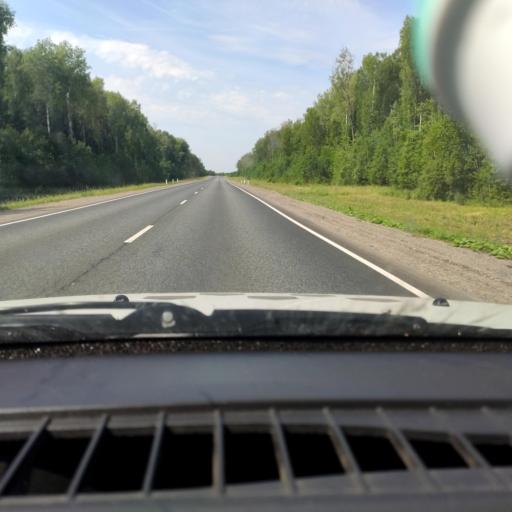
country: RU
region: Kirov
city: Kostino
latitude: 58.7440
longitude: 53.6177
